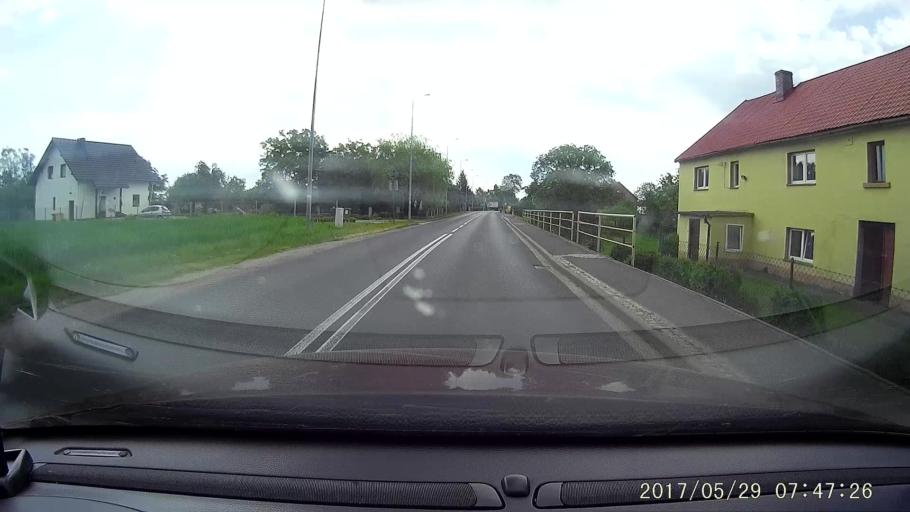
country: PL
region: Lower Silesian Voivodeship
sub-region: Powiat boleslawiecki
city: Boleslawiec
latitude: 51.2338
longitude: 15.6599
